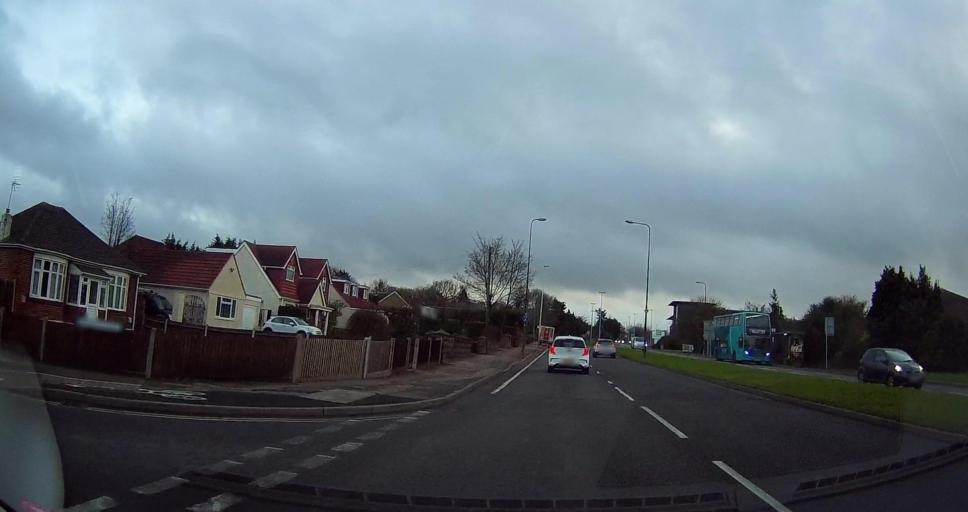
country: GB
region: England
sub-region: Kent
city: Chatham
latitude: 51.3493
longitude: 0.5082
